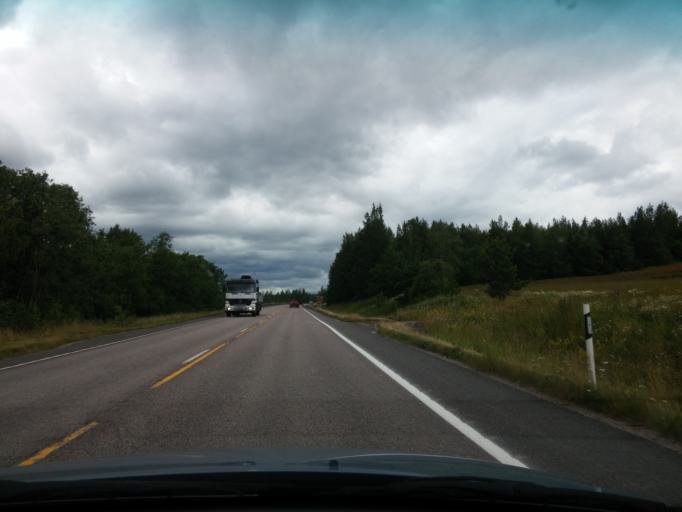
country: FI
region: Uusimaa
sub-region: Porvoo
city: Askola
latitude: 60.4663
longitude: 25.5738
